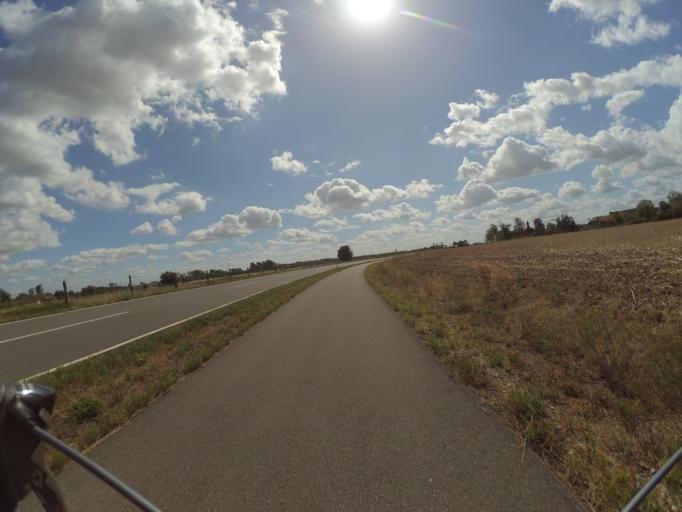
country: DE
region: North Rhine-Westphalia
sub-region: Regierungsbezirk Koln
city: Inden
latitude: 50.8889
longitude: 6.3778
